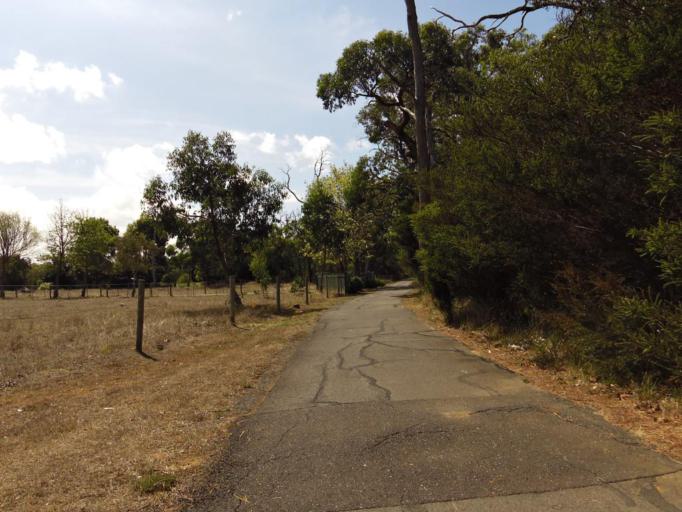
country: AU
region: Victoria
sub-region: Mornington Peninsula
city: Crib Point
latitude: -38.3480
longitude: 145.1695
